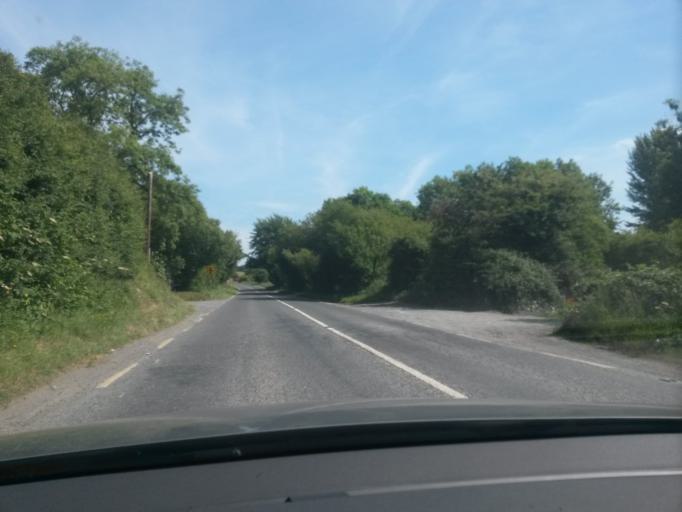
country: IE
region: Leinster
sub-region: Kildare
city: Johnstown
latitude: 53.2014
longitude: -6.6220
